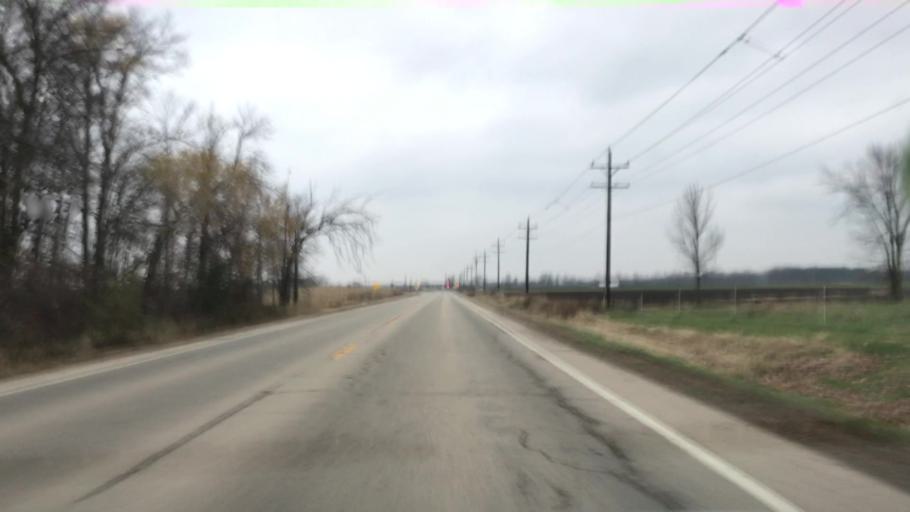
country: US
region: Wisconsin
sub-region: Outagamie County
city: Seymour
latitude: 44.4938
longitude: -88.2912
